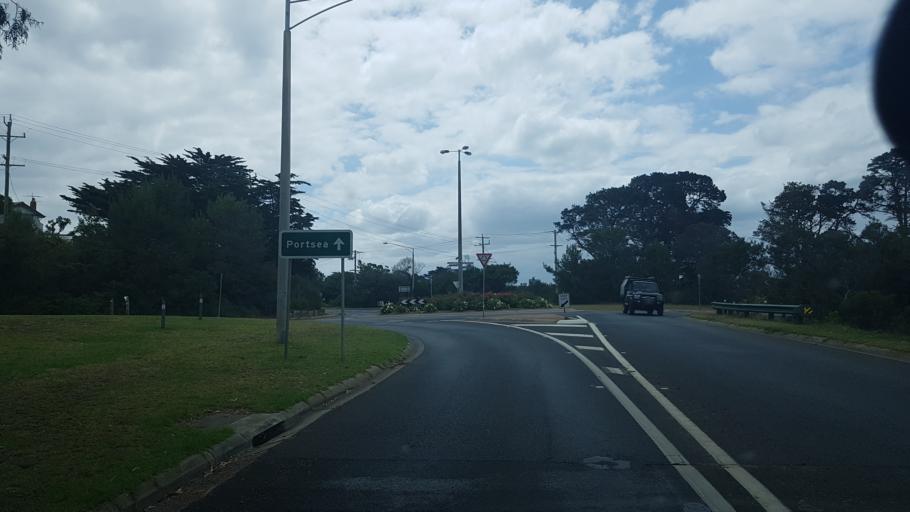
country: AU
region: Victoria
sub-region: Mornington Peninsula
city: Sorrento
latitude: -38.3359
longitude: 144.7343
